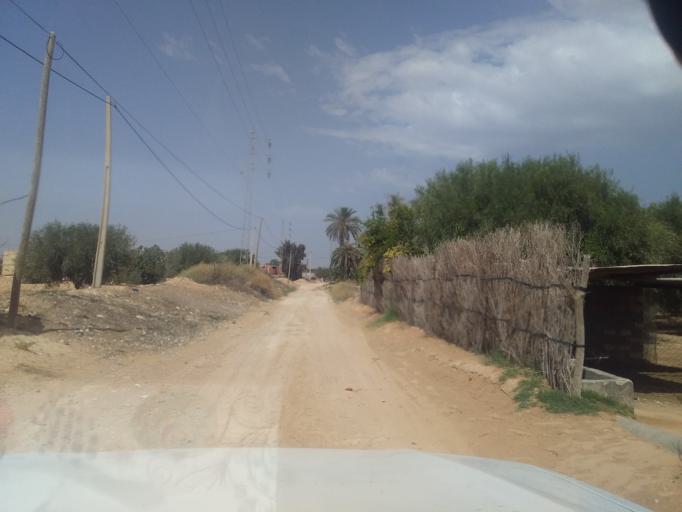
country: TN
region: Madanin
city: Medenine
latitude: 33.5924
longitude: 10.3266
